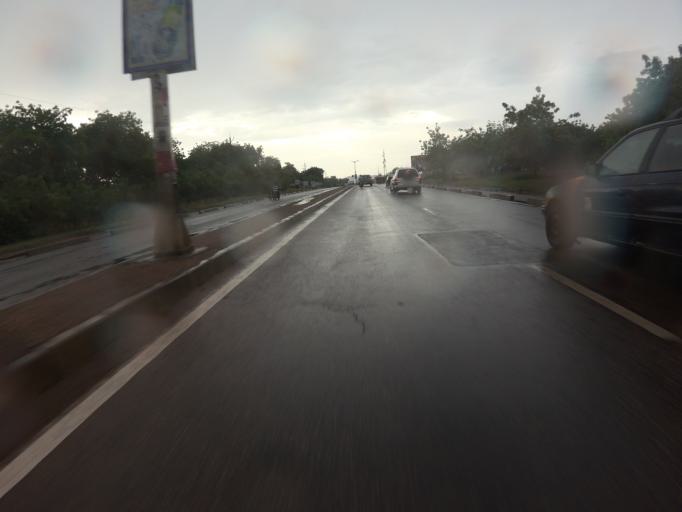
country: GH
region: Upper East
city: Bolgatanga
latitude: 10.7966
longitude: -0.8591
